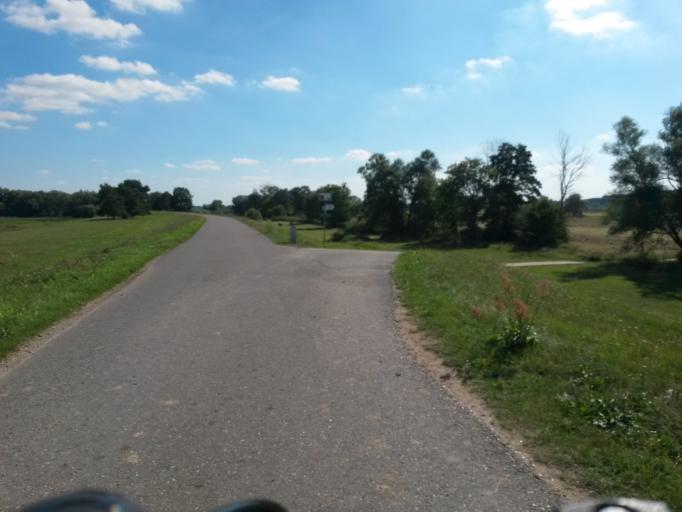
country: DE
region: Brandenburg
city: Schoneberg
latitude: 52.9489
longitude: 14.1362
